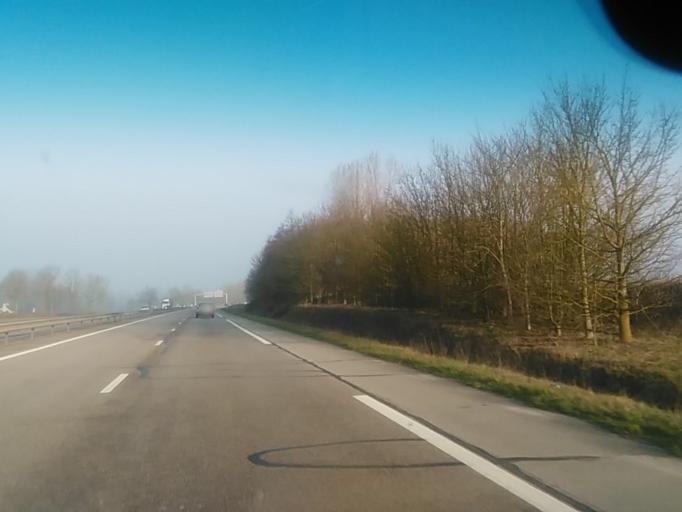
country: FR
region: Lower Normandy
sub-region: Departement du Calvados
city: Potigny
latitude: 48.9484
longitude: -0.2185
